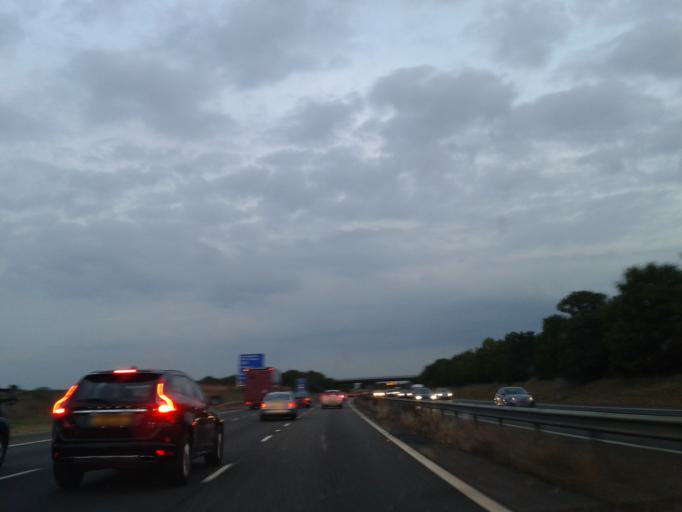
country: GB
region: England
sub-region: Oxfordshire
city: Somerton
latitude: 51.9650
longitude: -1.2322
